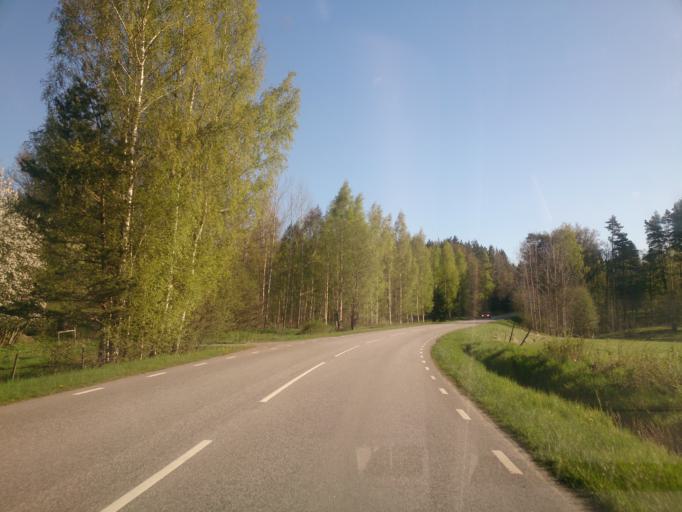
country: SE
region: OEstergoetland
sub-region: Linkopings Kommun
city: Berg
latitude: 58.5161
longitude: 15.5476
